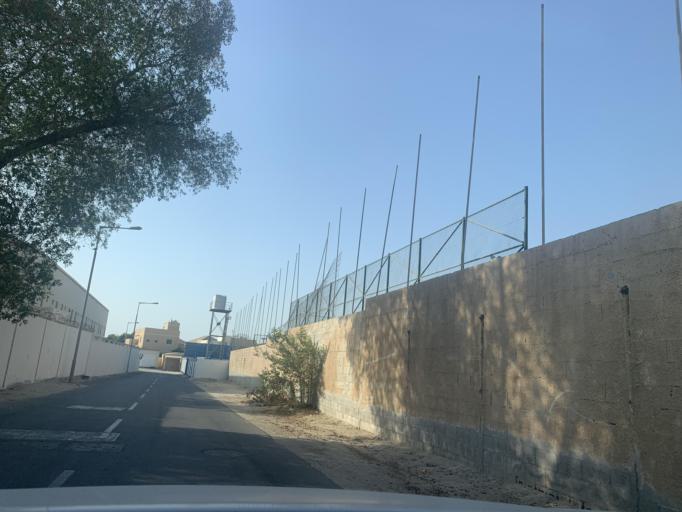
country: BH
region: Manama
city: Jidd Hafs
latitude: 26.1968
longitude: 50.4825
